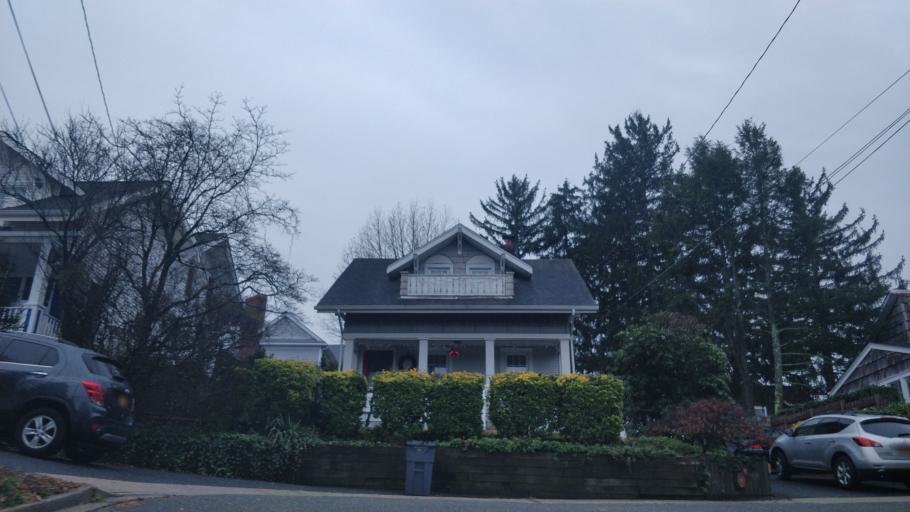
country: US
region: New York
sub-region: Nassau County
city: Glenwood Landing
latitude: 40.8284
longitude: -73.6428
